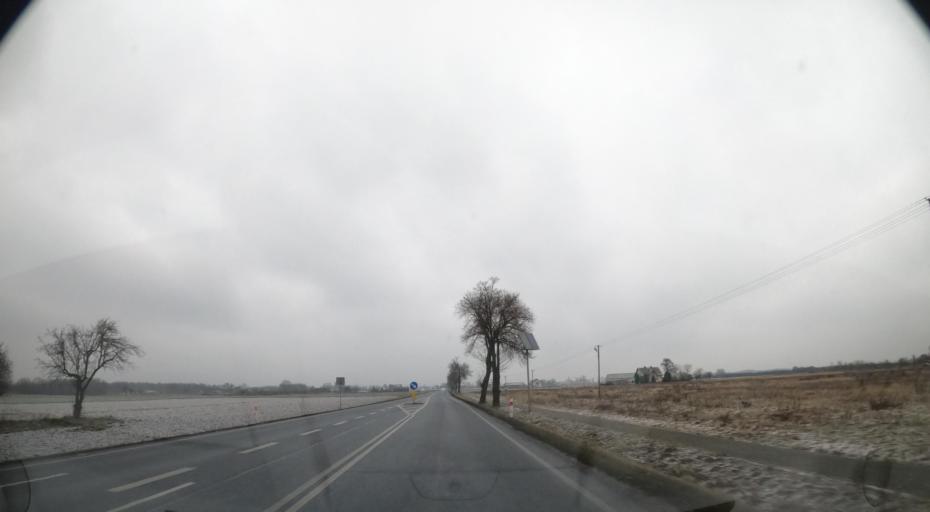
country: PL
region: Masovian Voivodeship
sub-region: Powiat sochaczewski
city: Mlodzieszyn
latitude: 52.2752
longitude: 20.1704
